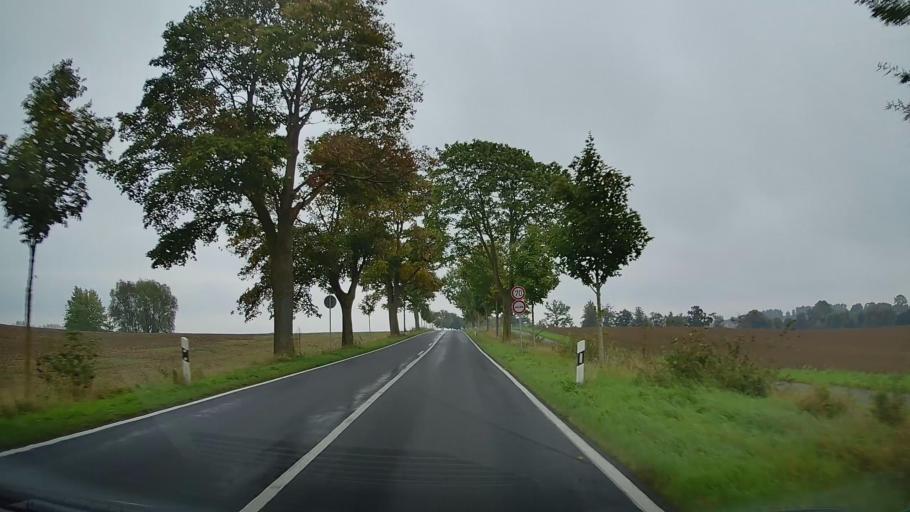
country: DE
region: Mecklenburg-Vorpommern
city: Ostseebad Boltenhagen
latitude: 53.9532
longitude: 11.2272
